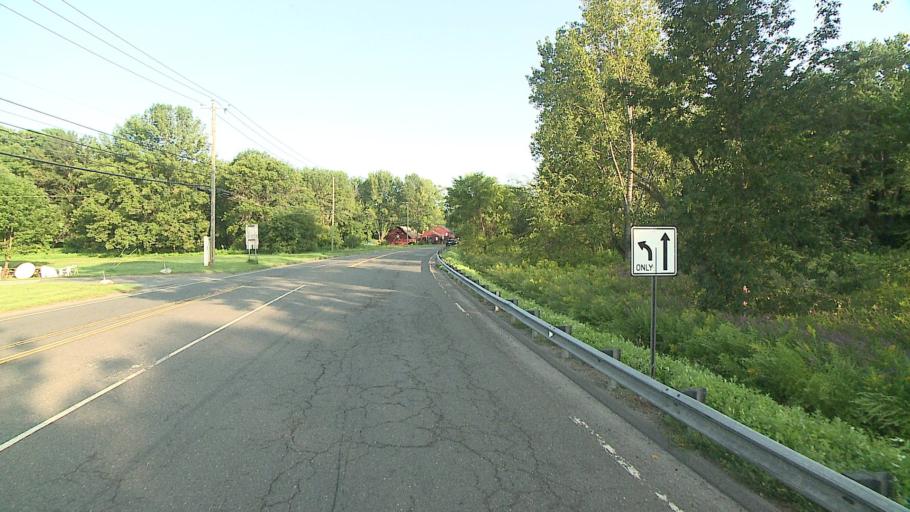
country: US
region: Connecticut
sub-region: Litchfield County
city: New Milford
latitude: 41.5755
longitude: -73.4192
